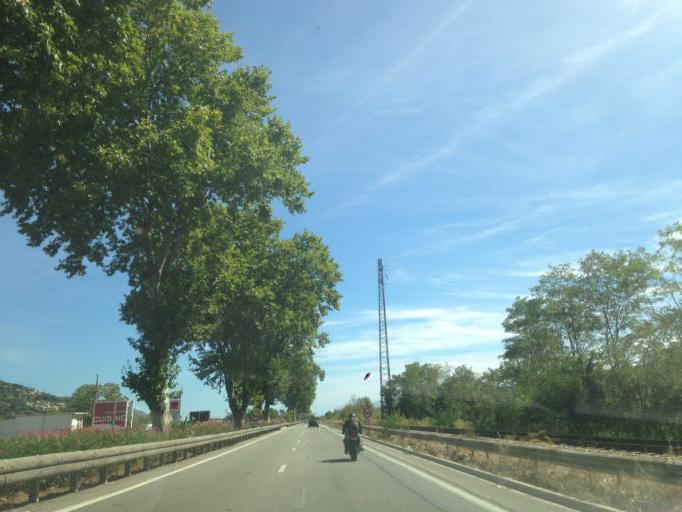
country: FR
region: Provence-Alpes-Cote d'Azur
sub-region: Departement des Alpes-Maritimes
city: Gattieres
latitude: 43.7358
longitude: 7.1842
